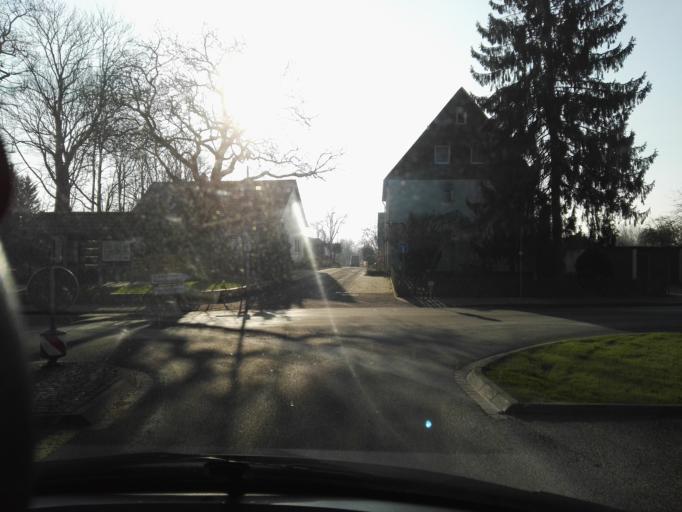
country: DE
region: Lower Saxony
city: Sarstedt
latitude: 52.2477
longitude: 9.8345
